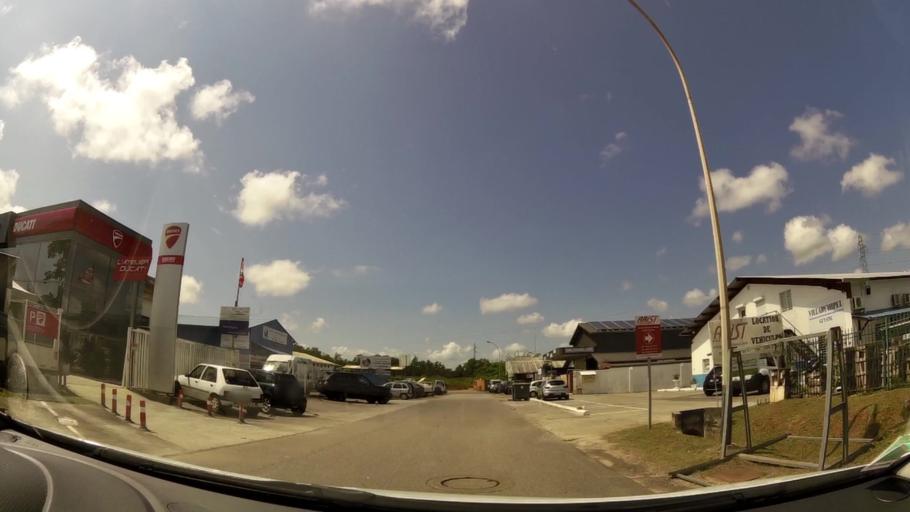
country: GF
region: Guyane
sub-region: Guyane
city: Cayenne
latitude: 4.9295
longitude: -52.3288
